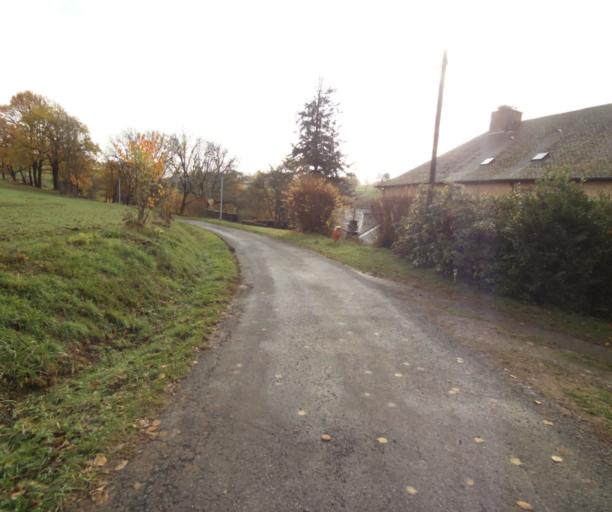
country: FR
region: Limousin
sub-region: Departement de la Correze
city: Sainte-Fereole
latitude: 45.2044
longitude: 1.6340
